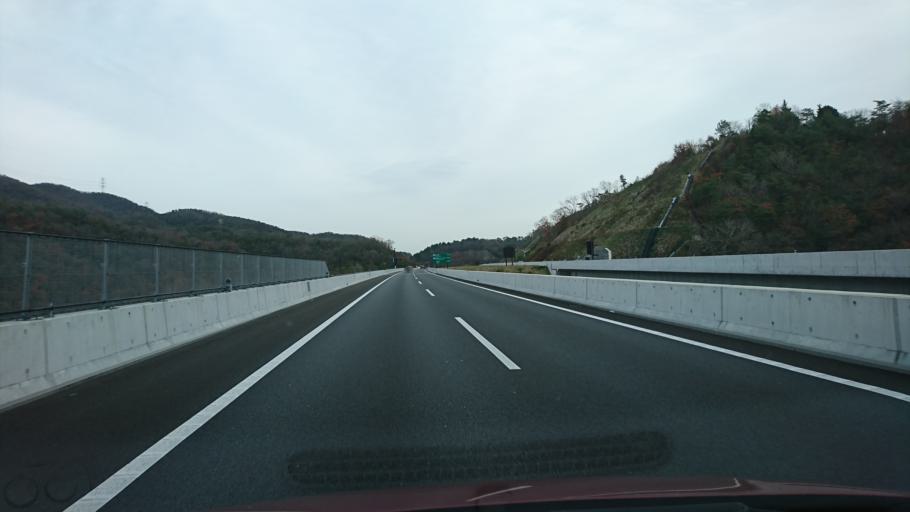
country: JP
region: Hyogo
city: Takarazuka
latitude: 34.8696
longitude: 135.3140
